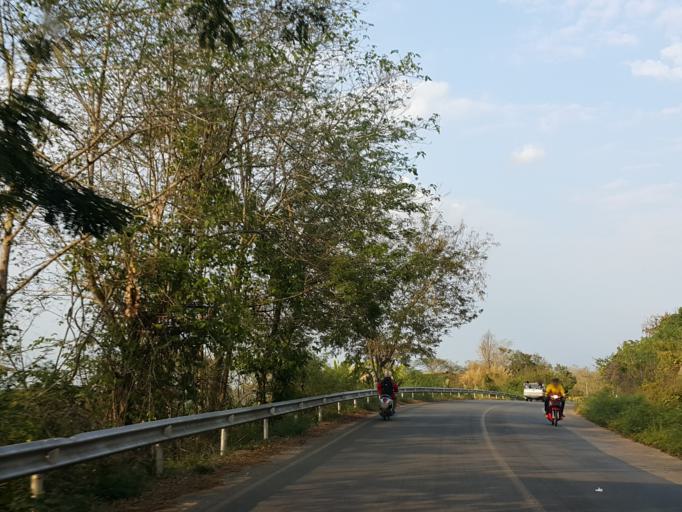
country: TH
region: Lampang
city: Hang Chat
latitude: 18.4471
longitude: 99.4522
